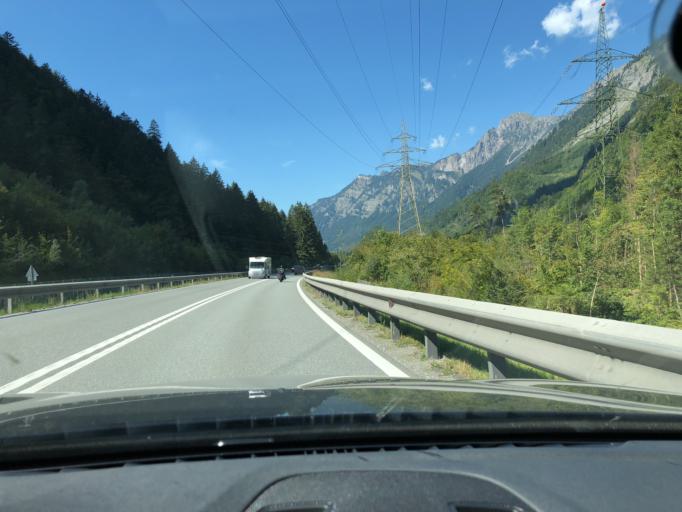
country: AT
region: Vorarlberg
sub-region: Politischer Bezirk Bludenz
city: Dalaas
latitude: 47.1303
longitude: 9.9569
